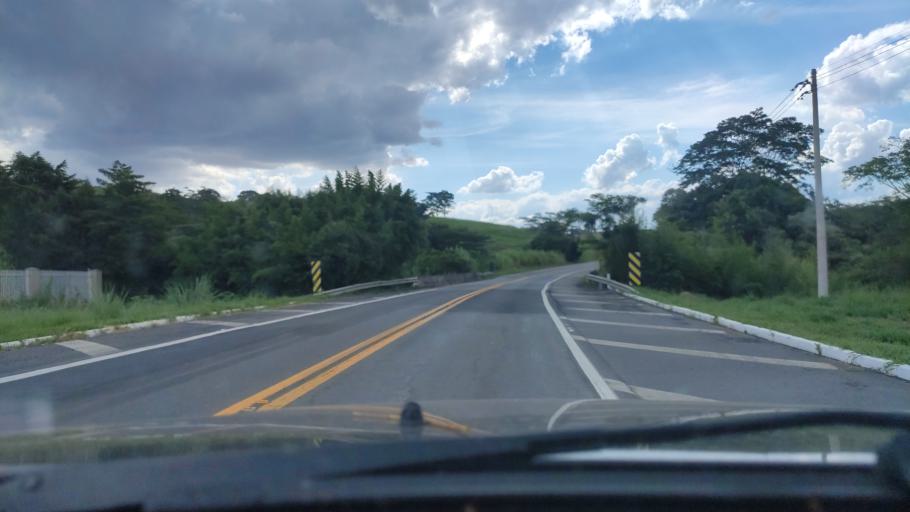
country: BR
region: Sao Paulo
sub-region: Aguas De Lindoia
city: Aguas de Lindoia
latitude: -22.4655
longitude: -46.7203
